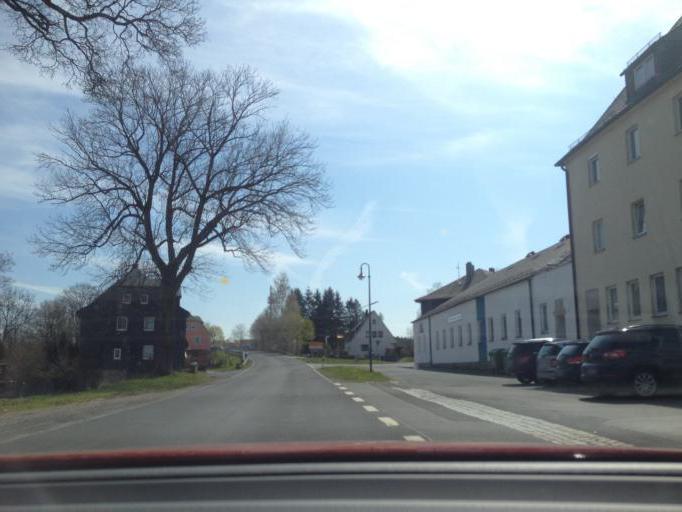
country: DE
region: Bavaria
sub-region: Upper Franconia
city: Roslau
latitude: 50.0787
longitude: 11.9847
